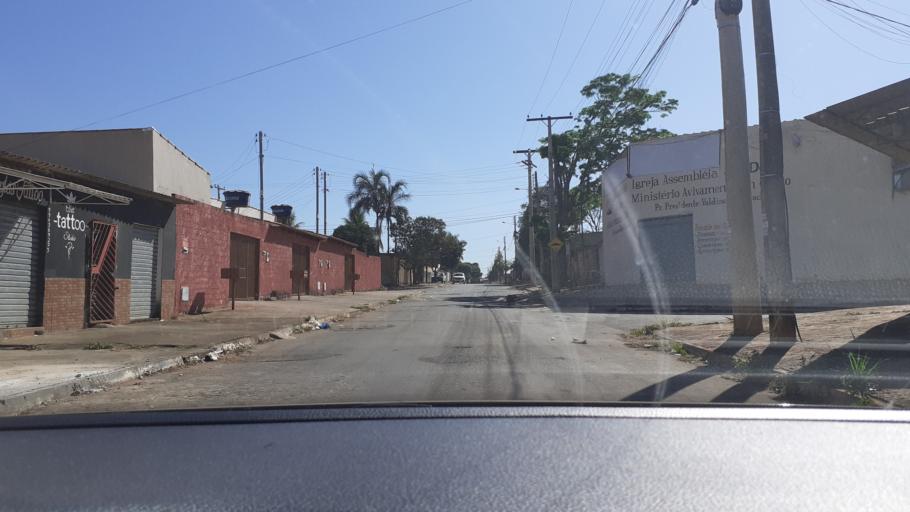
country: BR
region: Goias
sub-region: Aparecida De Goiania
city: Aparecida de Goiania
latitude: -16.8391
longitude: -49.2473
